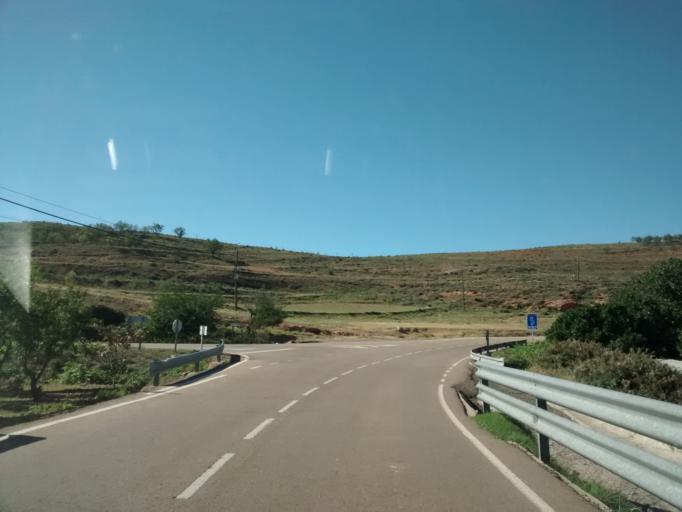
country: ES
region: Aragon
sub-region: Provincia de Zaragoza
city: Trasmoz
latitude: 41.8299
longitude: -1.7235
